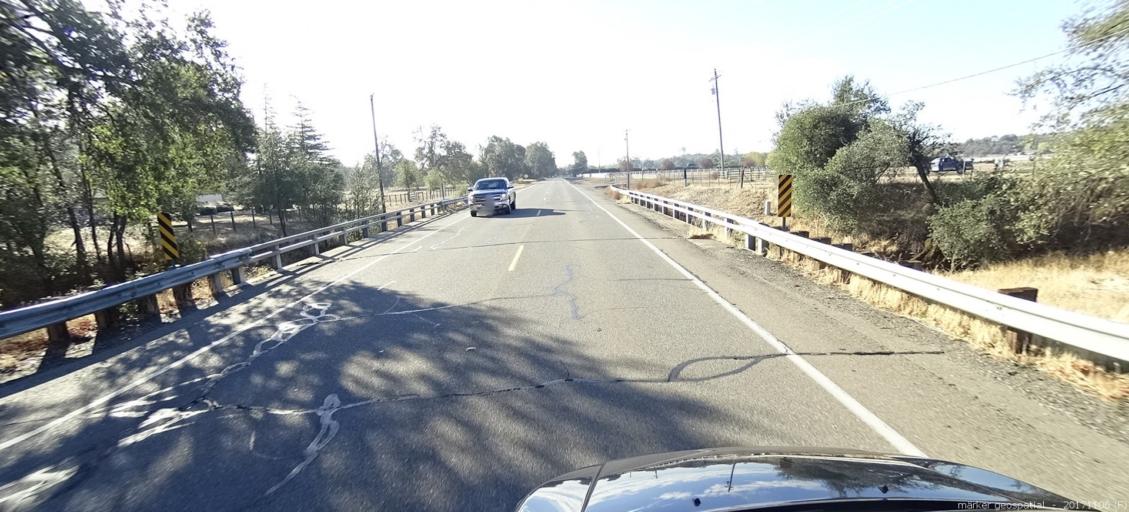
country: US
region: California
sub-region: Shasta County
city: Palo Cedro
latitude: 40.5310
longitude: -122.2390
